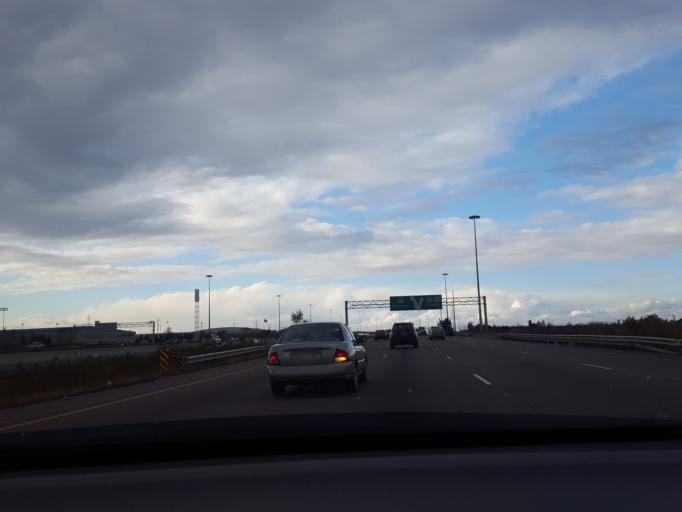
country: CA
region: Ontario
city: Mississauga
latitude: 43.6272
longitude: -79.6430
